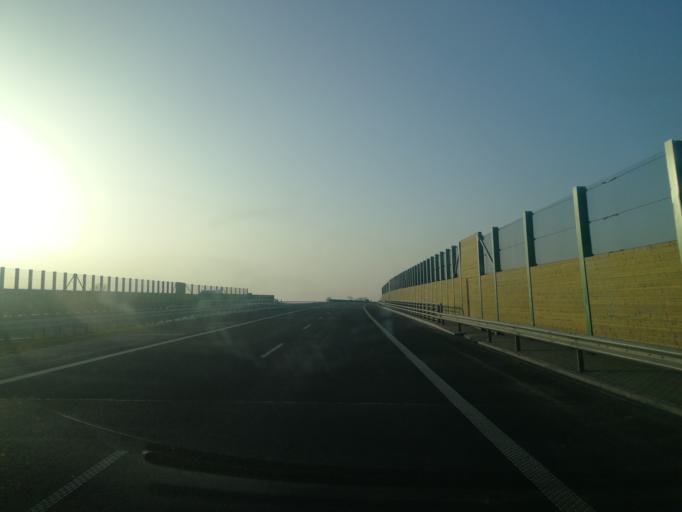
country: PL
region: Pomeranian Voivodeship
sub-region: Powiat nowodworski
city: Nowy Dwor Gdanski
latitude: 54.1738
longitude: 19.2003
